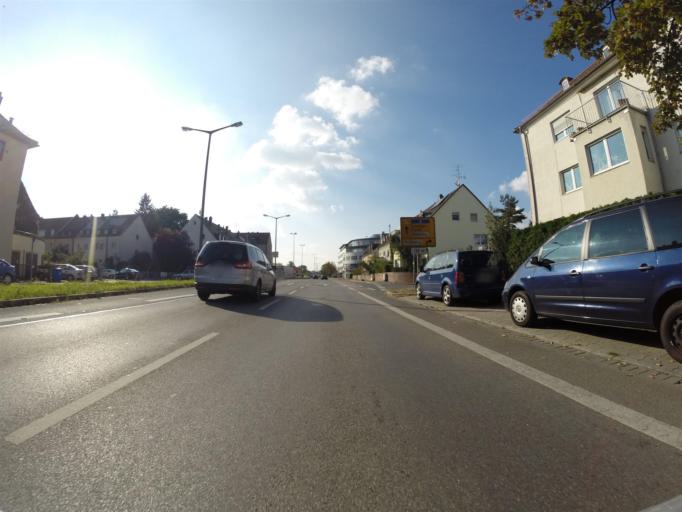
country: DE
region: Bavaria
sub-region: Regierungsbezirk Mittelfranken
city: Nuernberg
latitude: 49.4695
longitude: 11.0834
